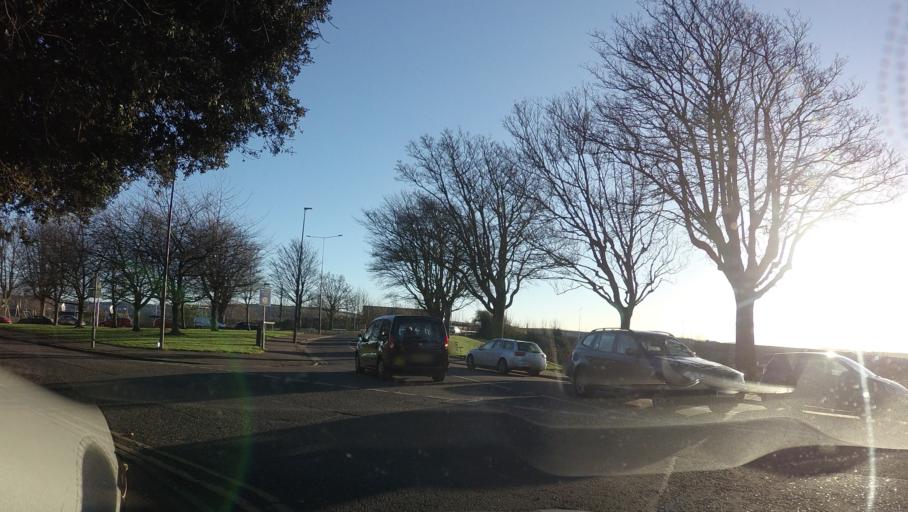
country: GB
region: Scotland
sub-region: Dundee City
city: Dundee
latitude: 56.4532
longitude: -2.9890
